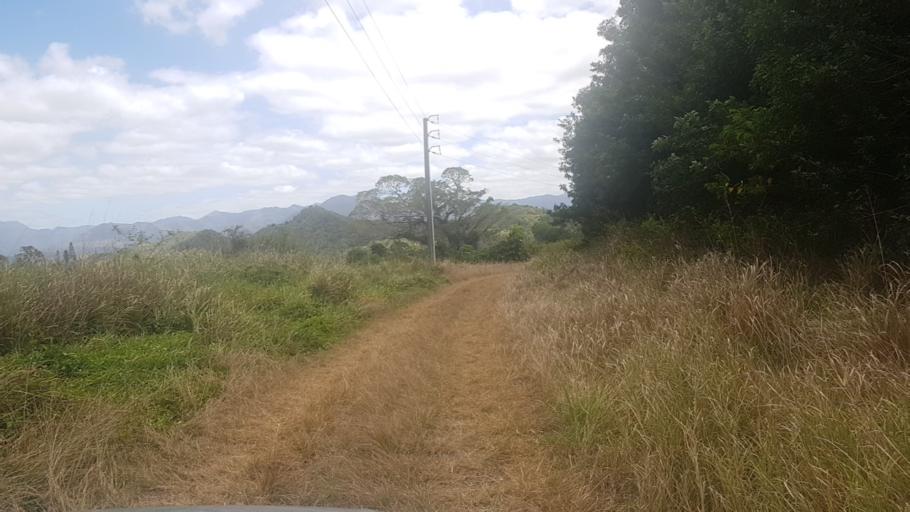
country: NC
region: South Province
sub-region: Dumbea
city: Dumbea
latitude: -22.1857
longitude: 166.4792
